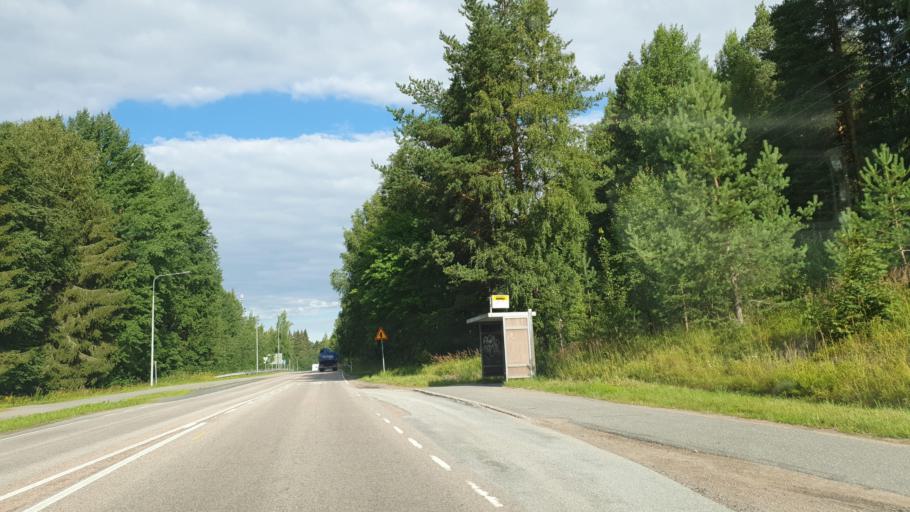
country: FI
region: Central Finland
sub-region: Jyvaeskylae
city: Saeynaetsalo
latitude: 62.1800
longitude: 25.7303
